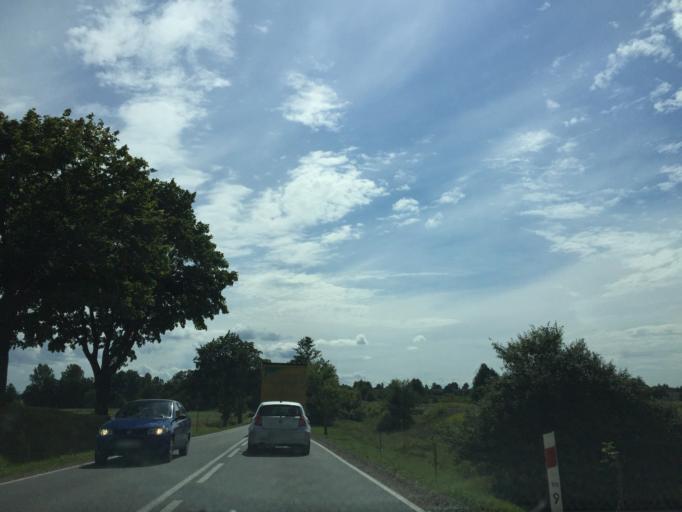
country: PL
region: Masovian Voivodeship
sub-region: Powiat losicki
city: Sarnaki
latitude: 52.3074
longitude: 22.8377
